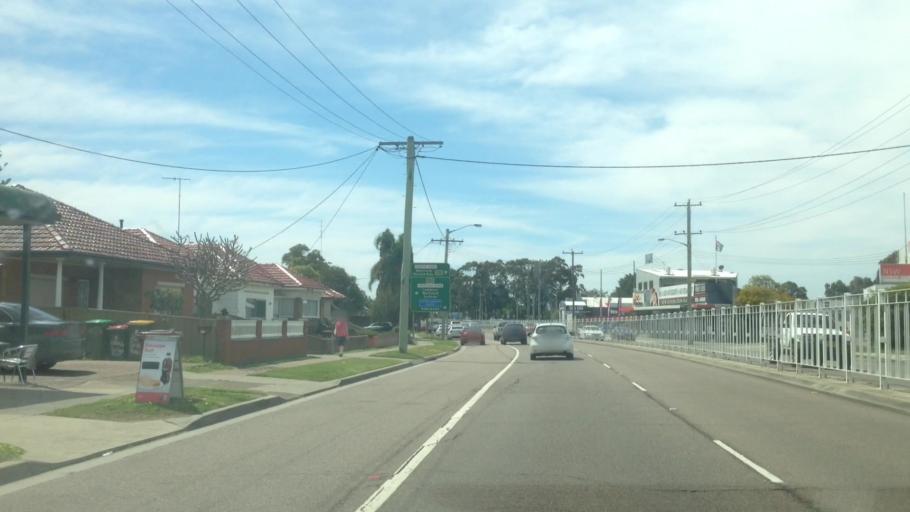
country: AU
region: New South Wales
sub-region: Newcastle
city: Broadmeadow
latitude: -32.9175
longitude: 151.7247
